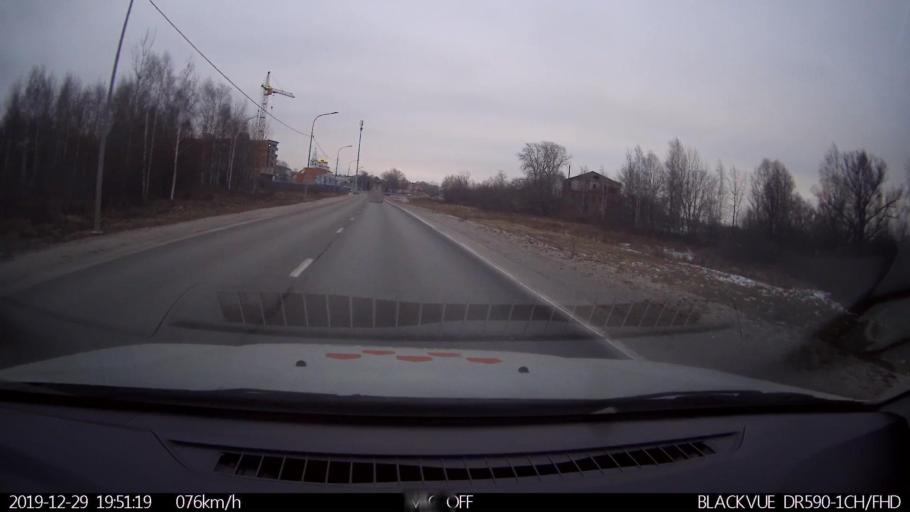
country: RU
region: Nizjnij Novgorod
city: Bor
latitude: 56.3604
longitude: 44.0389
